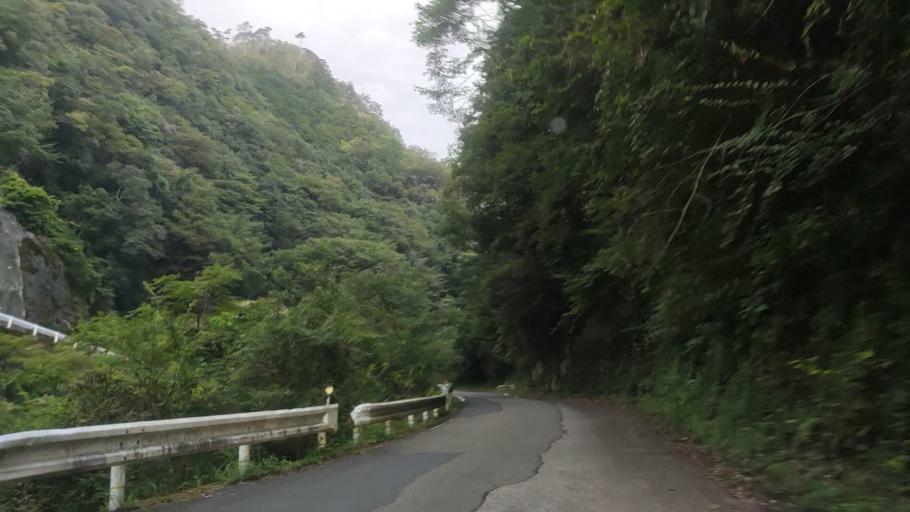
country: JP
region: Wakayama
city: Hashimoto
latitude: 34.2782
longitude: 135.6313
